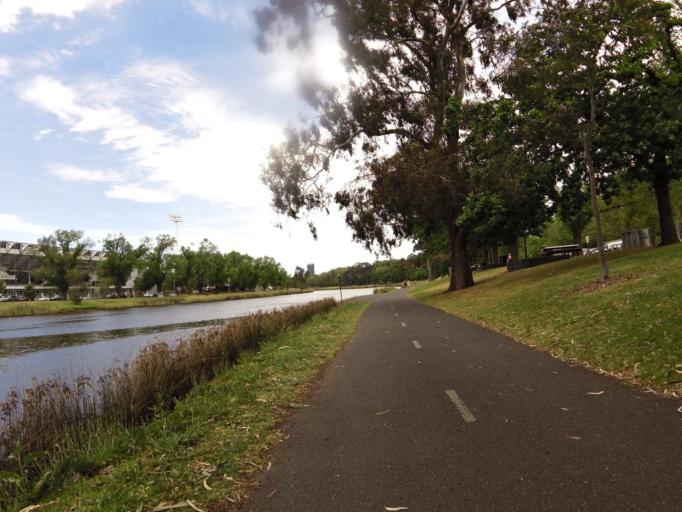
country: AU
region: Victoria
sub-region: Melbourne
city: East Melbourne
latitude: -37.8238
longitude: 144.9773
